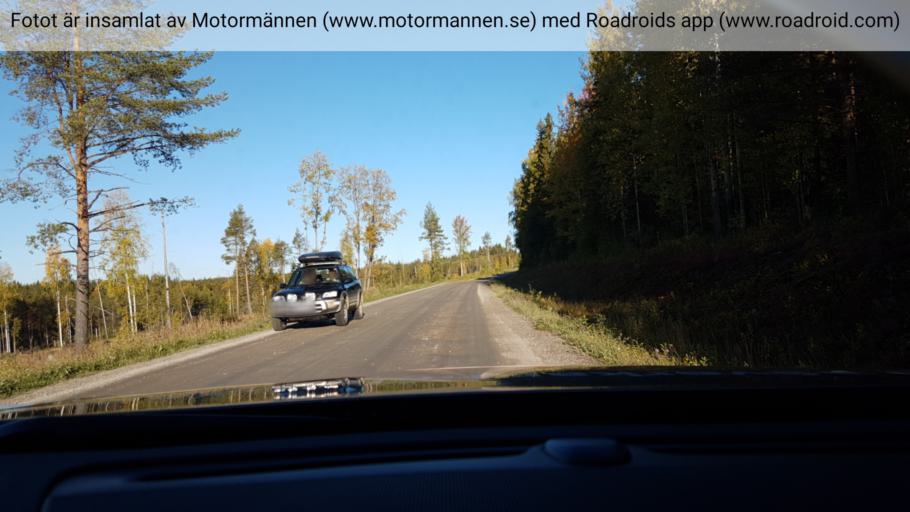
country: SE
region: Norrbotten
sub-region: Alvsbyns Kommun
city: AElvsbyn
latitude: 66.1904
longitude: 21.1973
